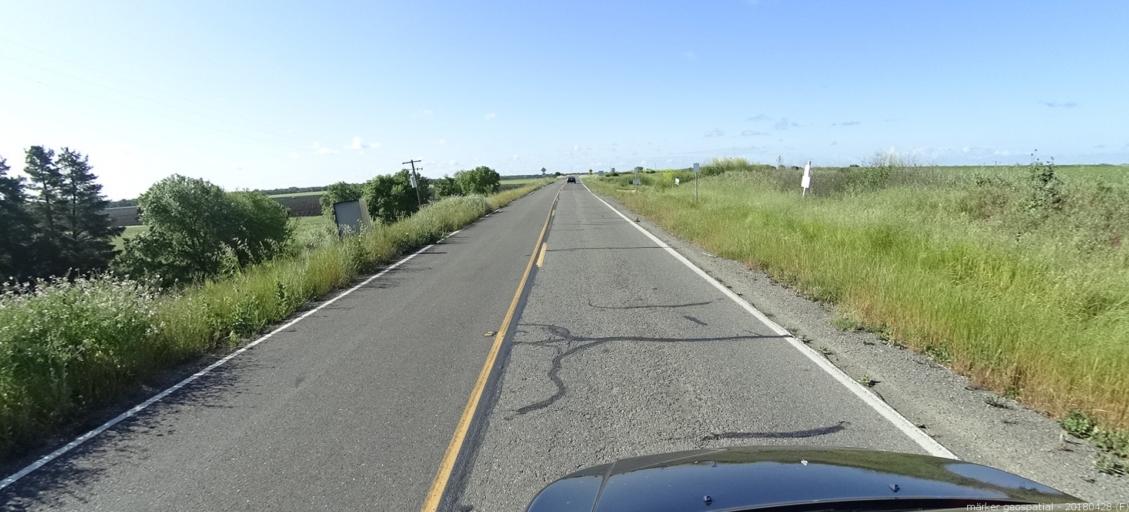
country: US
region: California
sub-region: Yolo County
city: West Sacramento
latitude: 38.5044
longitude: -121.5822
